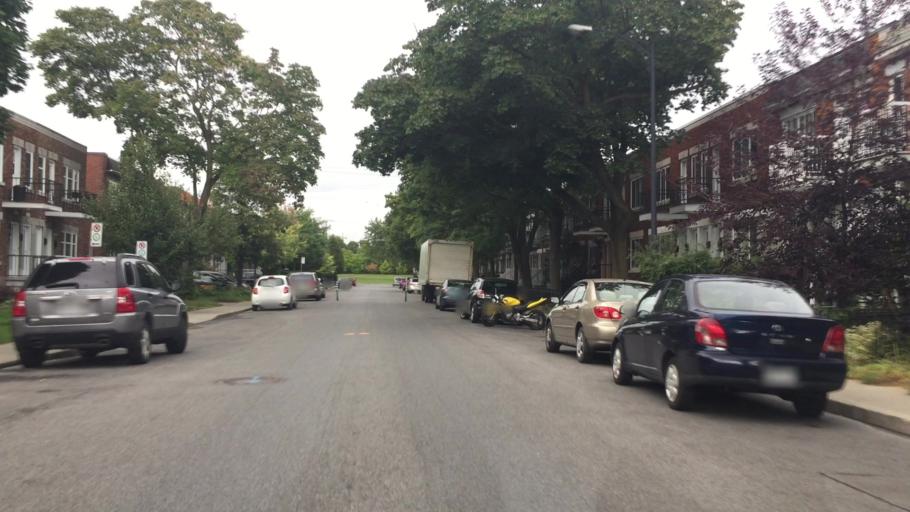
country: CA
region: Quebec
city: Saint-Raymond
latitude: 45.4465
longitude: -73.5869
